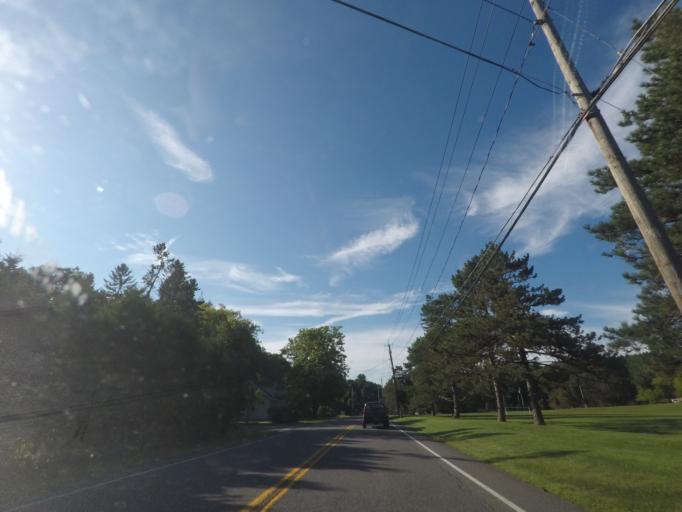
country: US
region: New York
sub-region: Albany County
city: West Albany
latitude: 42.7191
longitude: -73.7691
